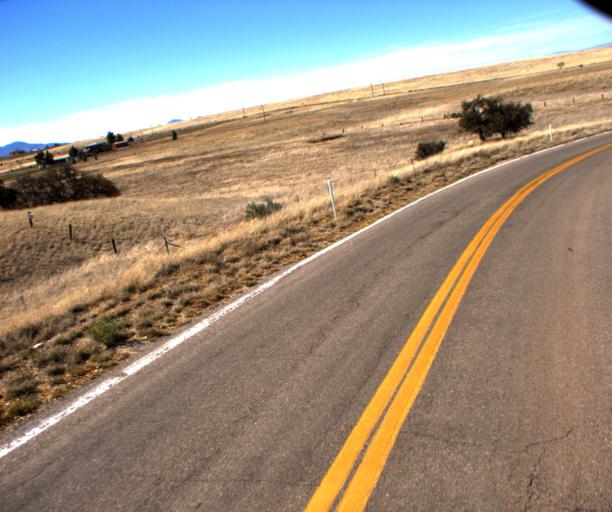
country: US
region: Arizona
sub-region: Cochise County
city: Huachuca City
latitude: 31.6051
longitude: -110.5790
